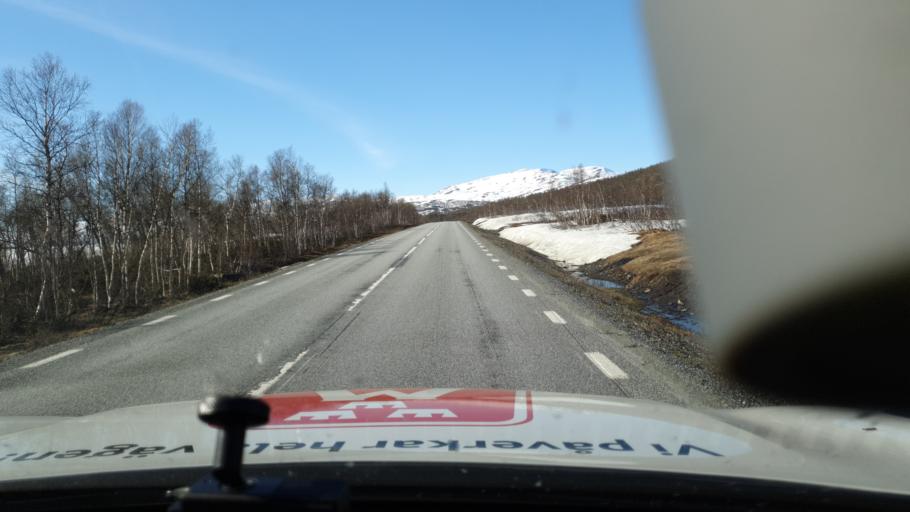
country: NO
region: Nordland
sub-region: Rana
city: Mo i Rana
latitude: 66.0734
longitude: 14.8726
